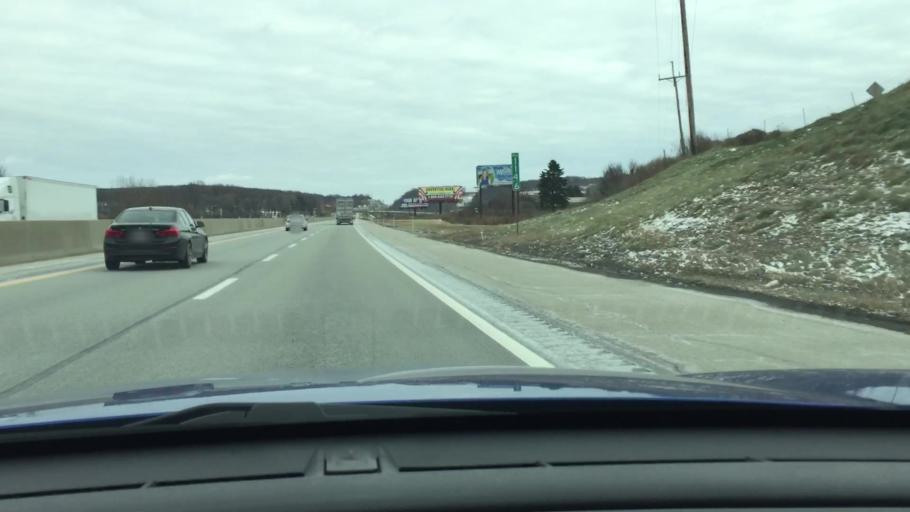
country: US
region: Pennsylvania
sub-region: Somerset County
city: Friedens
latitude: 39.9923
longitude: -79.0048
